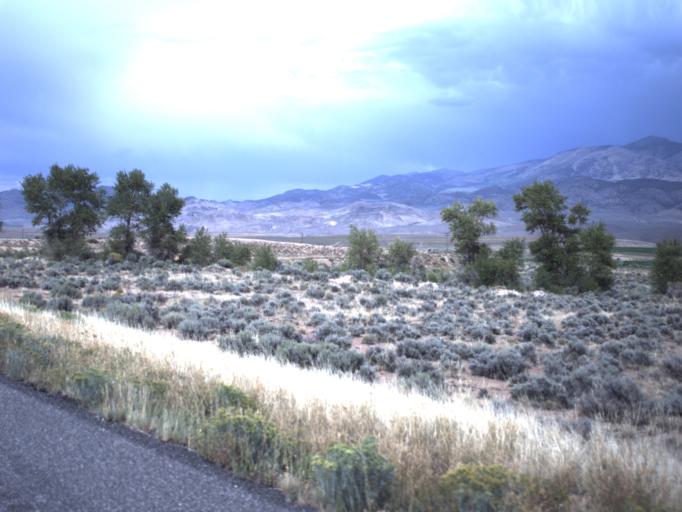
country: US
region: Utah
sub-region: Piute County
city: Junction
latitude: 38.3826
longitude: -112.2286
